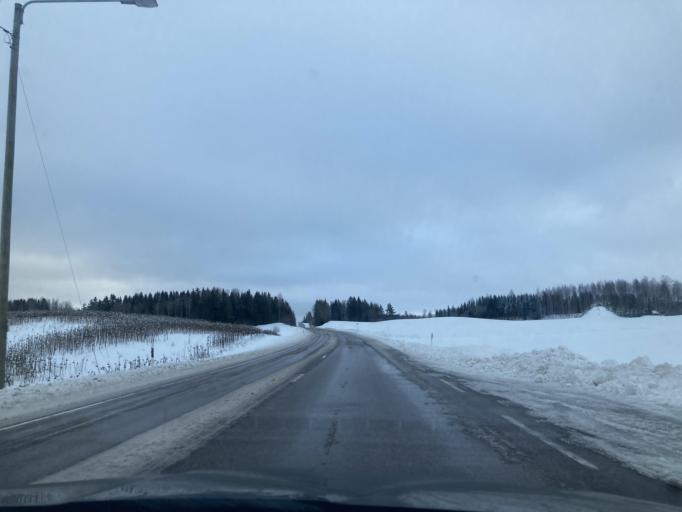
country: FI
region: Paijanne Tavastia
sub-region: Lahti
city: Asikkala
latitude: 61.2090
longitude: 25.3781
